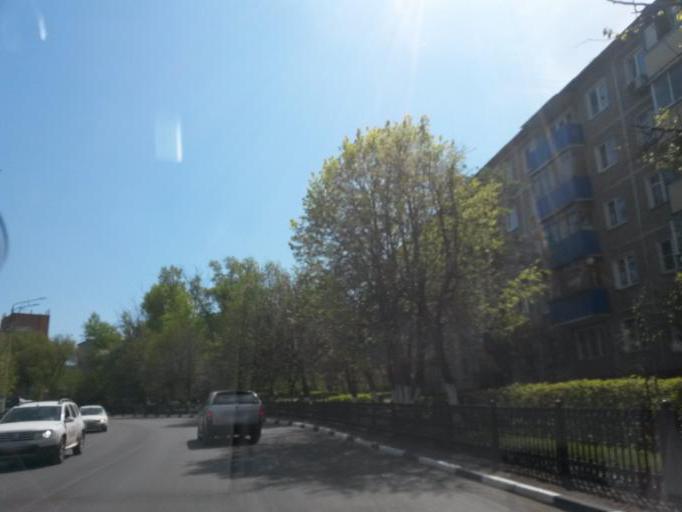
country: RU
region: Moskovskaya
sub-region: Podol'skiy Rayon
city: Podol'sk
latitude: 55.4211
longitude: 37.5304
